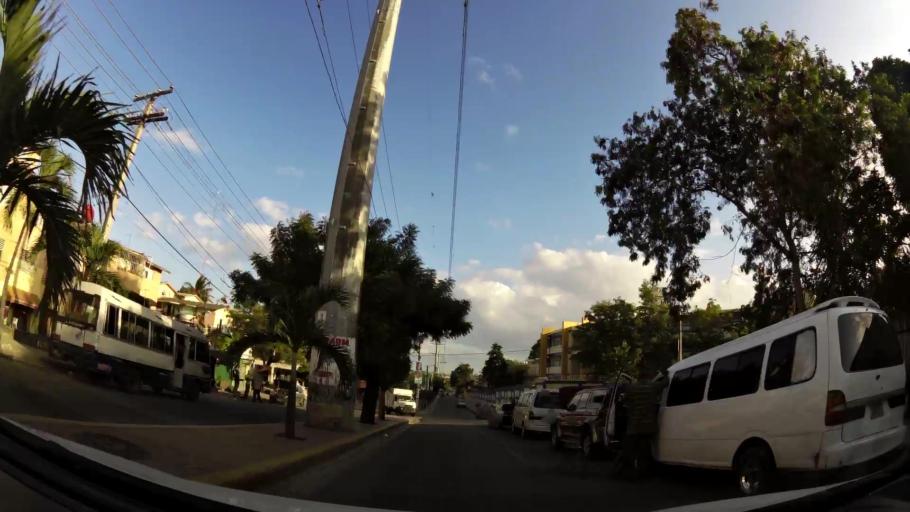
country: DO
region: Nacional
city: La Agustina
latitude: 18.5426
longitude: -69.9282
